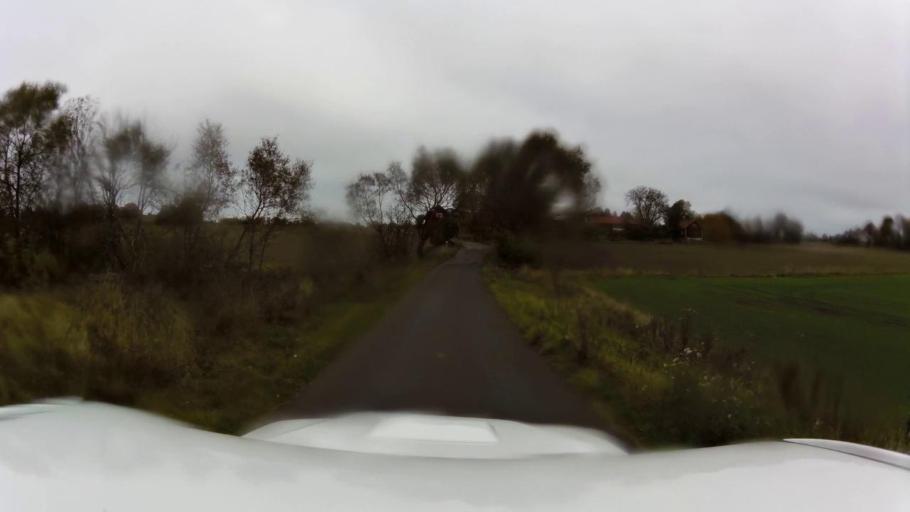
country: SE
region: OEstergoetland
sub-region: Linkopings Kommun
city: Linghem
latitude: 58.4898
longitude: 15.7424
